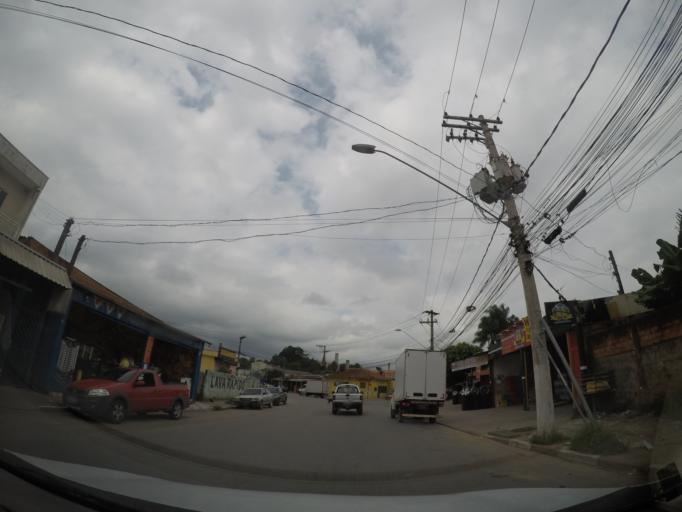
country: BR
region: Sao Paulo
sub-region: Aruja
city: Aruja
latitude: -23.4016
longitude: -46.4012
